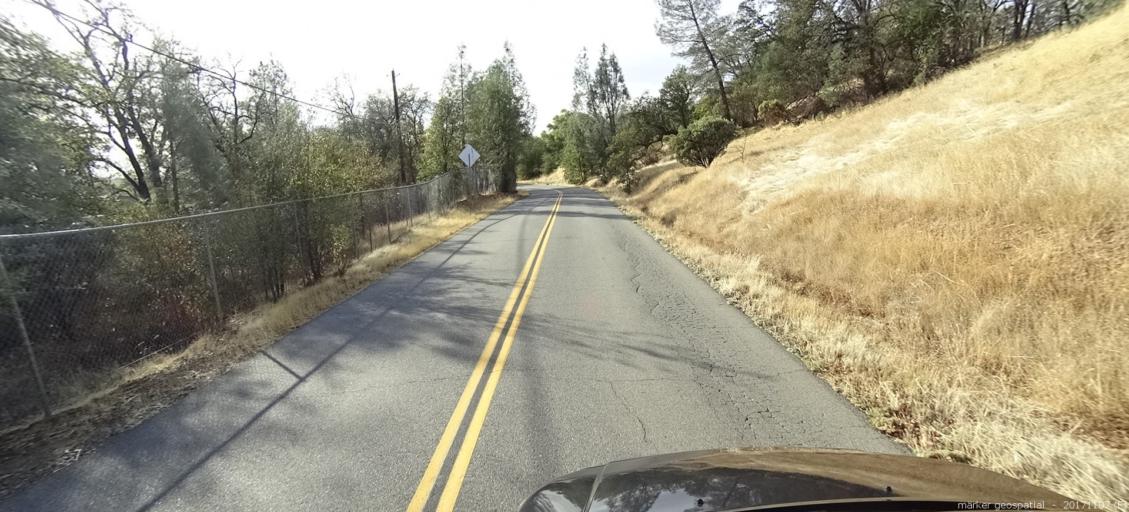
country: US
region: California
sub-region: Shasta County
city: Redding
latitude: 40.5029
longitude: -122.4482
